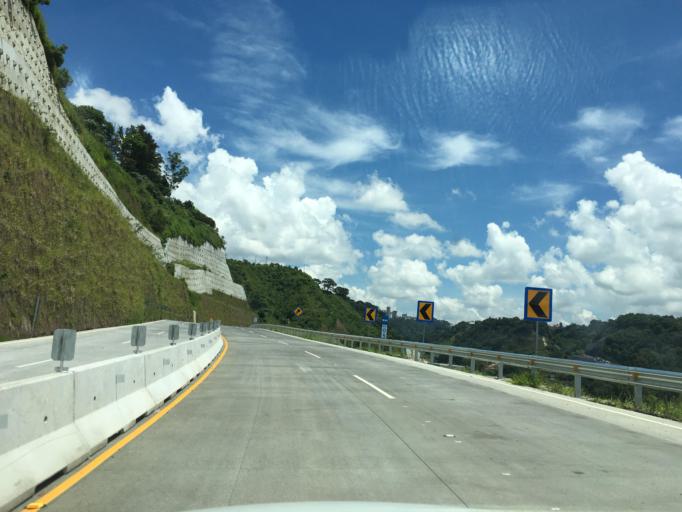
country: GT
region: Guatemala
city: Petapa
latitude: 14.5397
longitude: -90.5348
